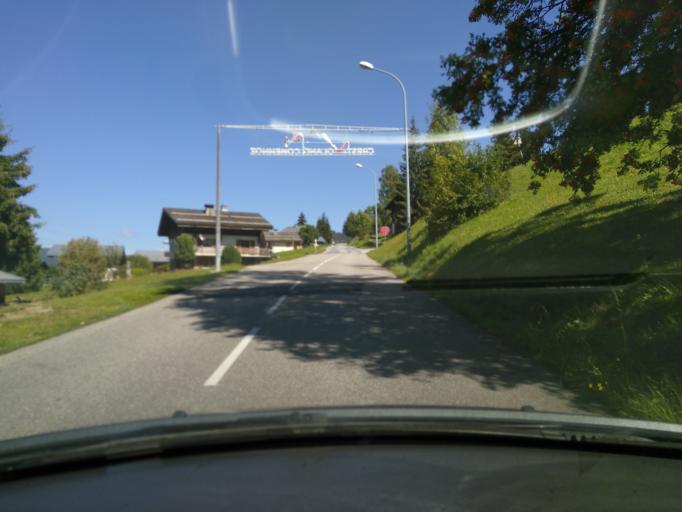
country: FR
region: Rhone-Alpes
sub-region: Departement de la Haute-Savoie
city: Praz-sur-Arly
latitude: 45.7965
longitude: 6.5119
